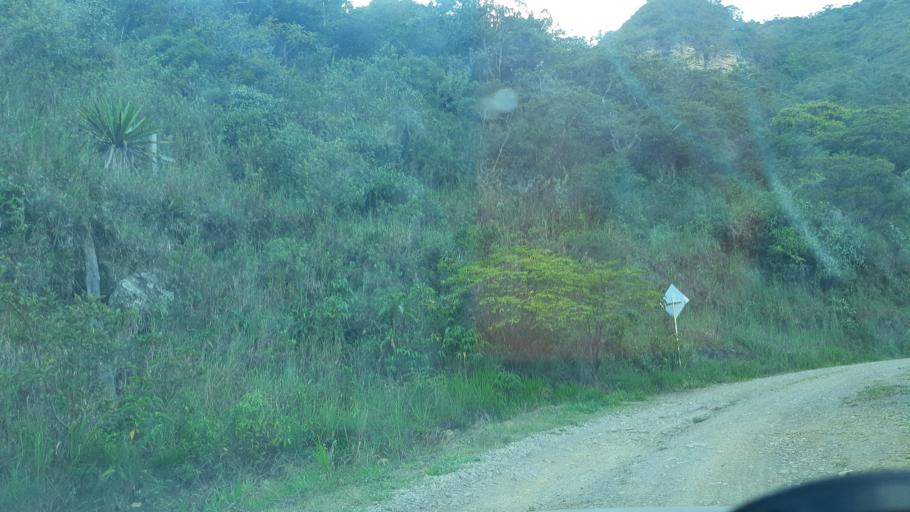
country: CO
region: Boyaca
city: Santa Sofia
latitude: 5.7442
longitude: -73.5782
